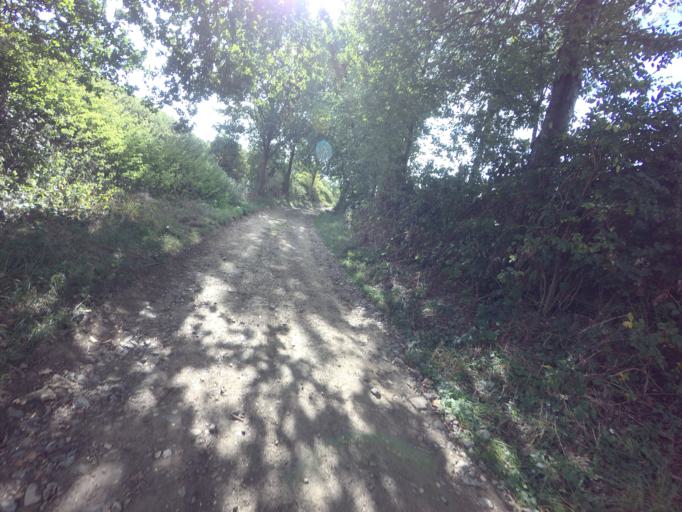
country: NL
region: Limburg
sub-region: Valkenburg aan de Geul
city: Schin op Geul
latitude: 50.8416
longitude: 5.9034
